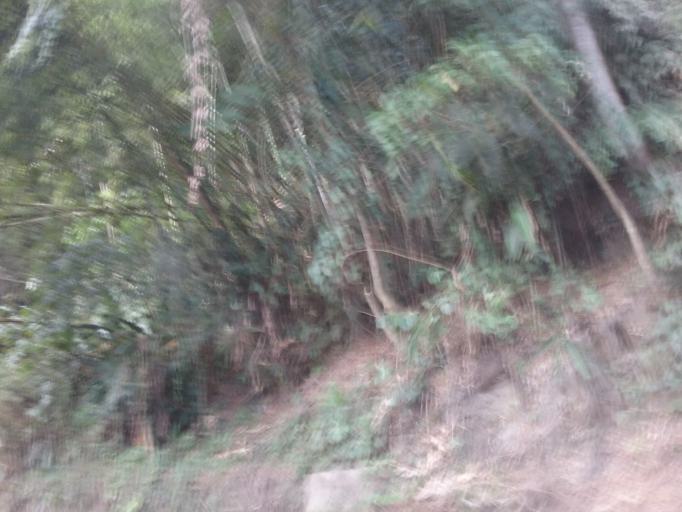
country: CO
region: Tolima
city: Libano
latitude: 4.8874
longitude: -75.0232
